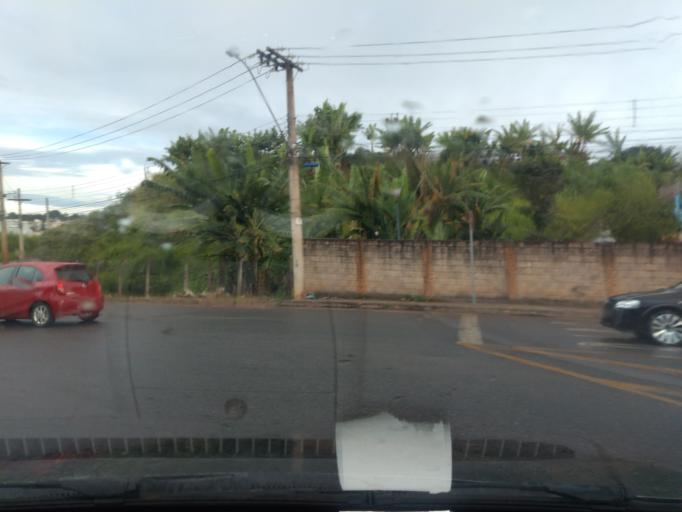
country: BR
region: Minas Gerais
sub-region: Varginha
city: Varginha
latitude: -21.5739
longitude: -45.4510
